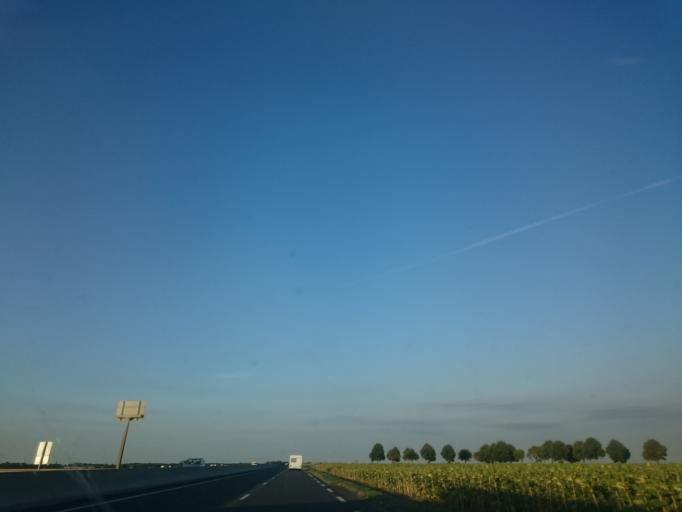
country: FR
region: Ile-de-France
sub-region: Departement de l'Essonne
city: Mereville
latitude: 48.3529
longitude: 2.0494
